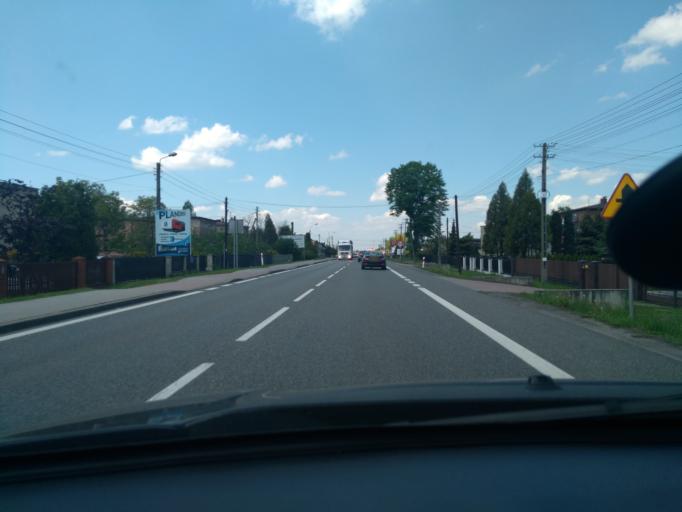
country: PL
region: Silesian Voivodeship
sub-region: Ruda Slaska
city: Ruda Slaska
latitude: 50.2156
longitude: 18.8384
